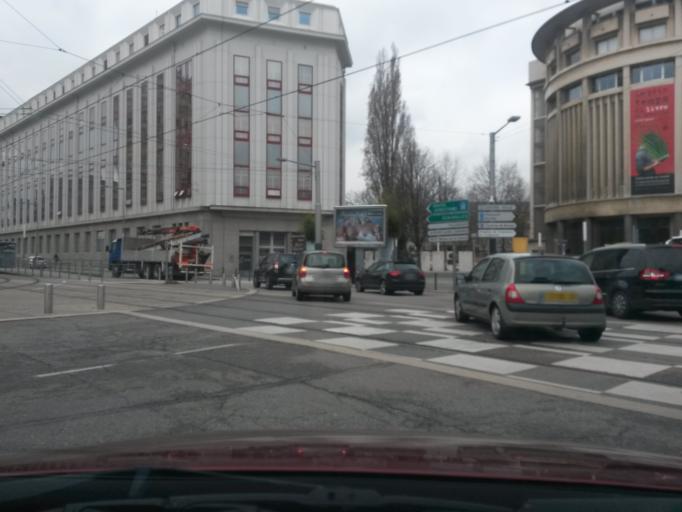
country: FR
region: Rhone-Alpes
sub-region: Departement de l'Isere
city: La Tronche
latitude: 45.1854
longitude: 5.7320
